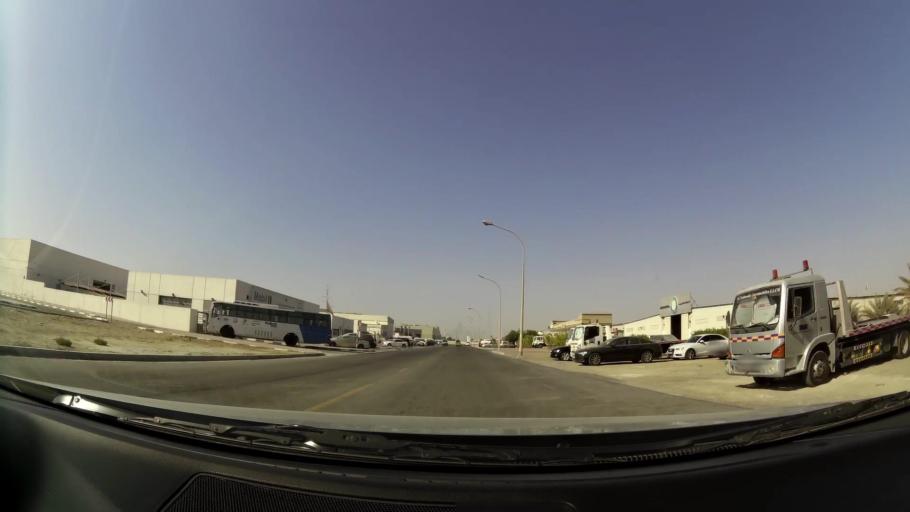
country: AE
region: Dubai
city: Dubai
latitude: 25.1361
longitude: 55.2184
